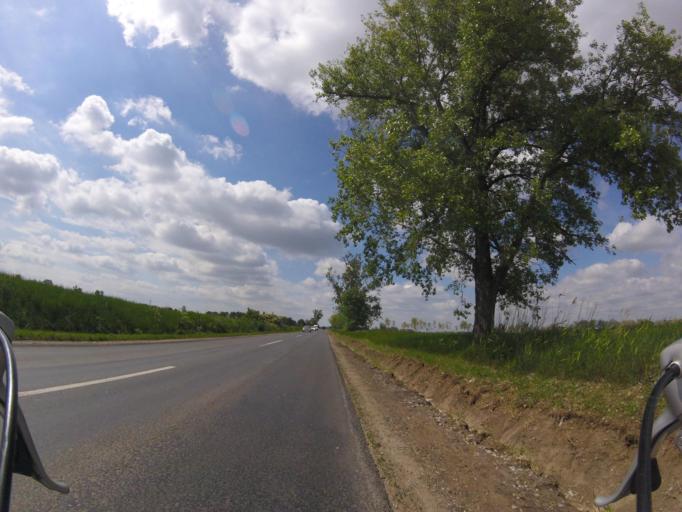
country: HU
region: Fejer
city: Soponya
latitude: 47.0424
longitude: 18.4319
